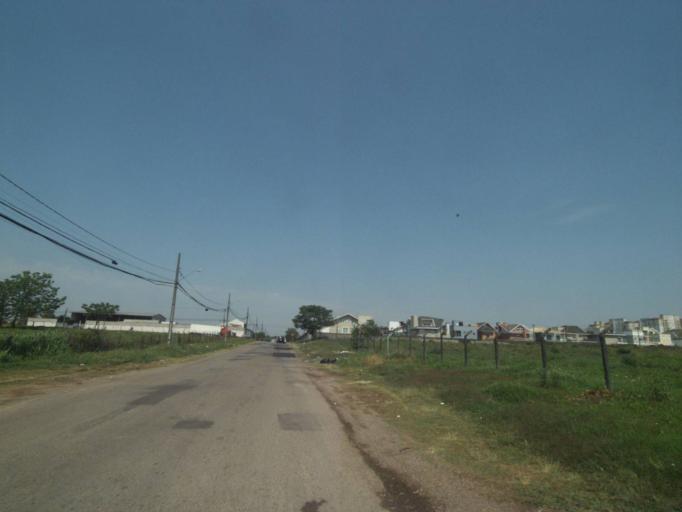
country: BR
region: Parana
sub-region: Sao Jose Dos Pinhais
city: Sao Jose dos Pinhais
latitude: -25.5144
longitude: -49.2811
